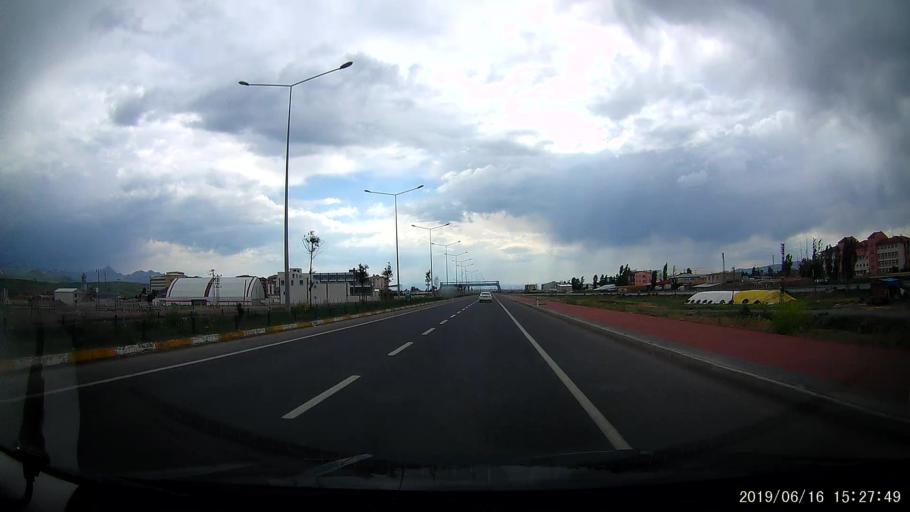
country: TR
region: Erzurum
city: Horasan
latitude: 40.0334
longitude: 42.1521
